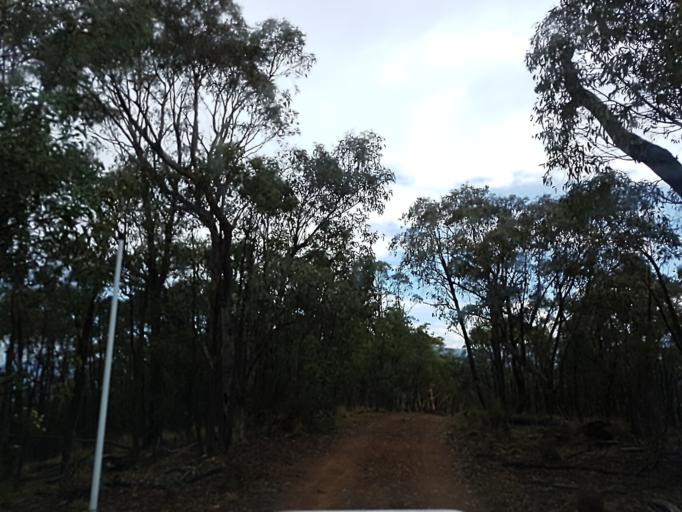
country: AU
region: New South Wales
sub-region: Snowy River
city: Jindabyne
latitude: -36.9047
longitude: 148.3419
